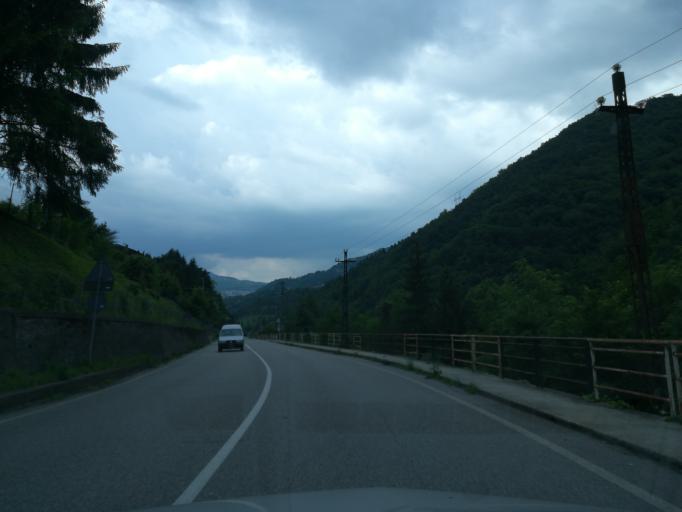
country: IT
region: Lombardy
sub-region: Provincia di Bergamo
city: Strozza
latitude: 45.7751
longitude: 9.5808
